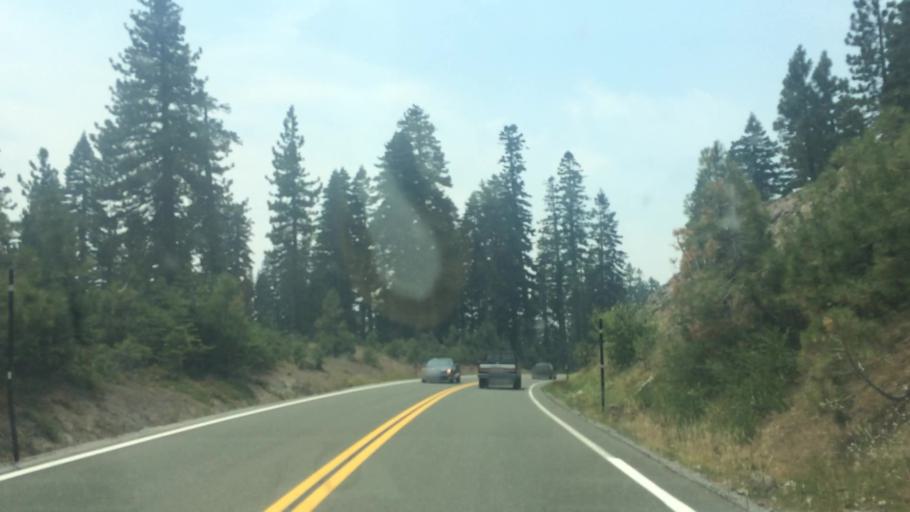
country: US
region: California
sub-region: Calaveras County
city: Arnold
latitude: 38.5826
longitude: -120.2520
